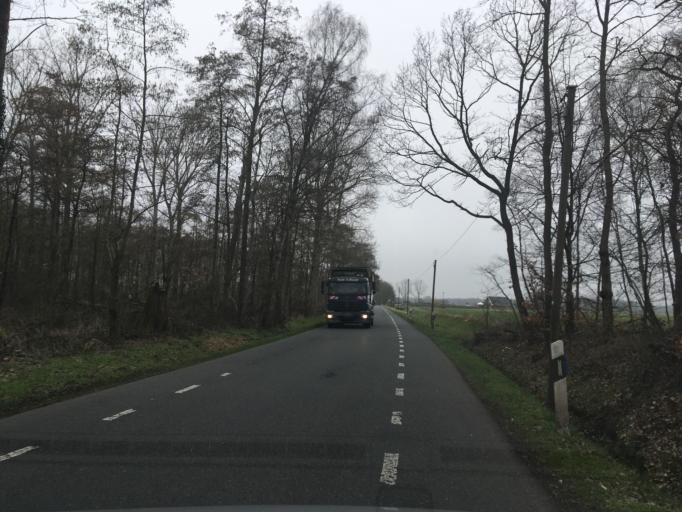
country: DE
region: North Rhine-Westphalia
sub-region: Regierungsbezirk Munster
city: Rhede
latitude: 51.8866
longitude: 6.7200
